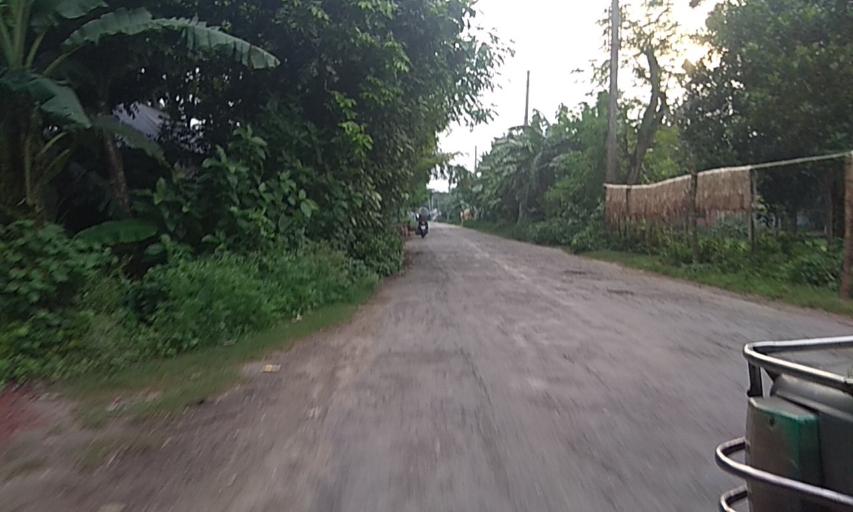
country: BD
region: Dhaka
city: Faridpur
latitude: 23.4586
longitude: 89.9777
